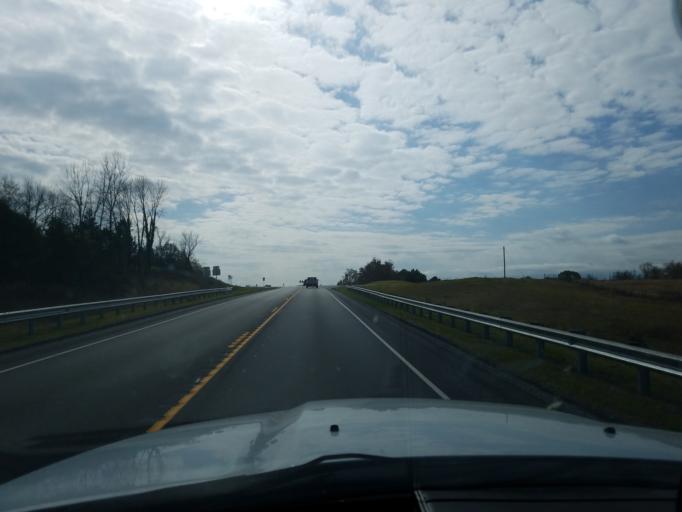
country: US
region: Kentucky
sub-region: Bullitt County
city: Mount Washington
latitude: 37.9722
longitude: -85.4916
